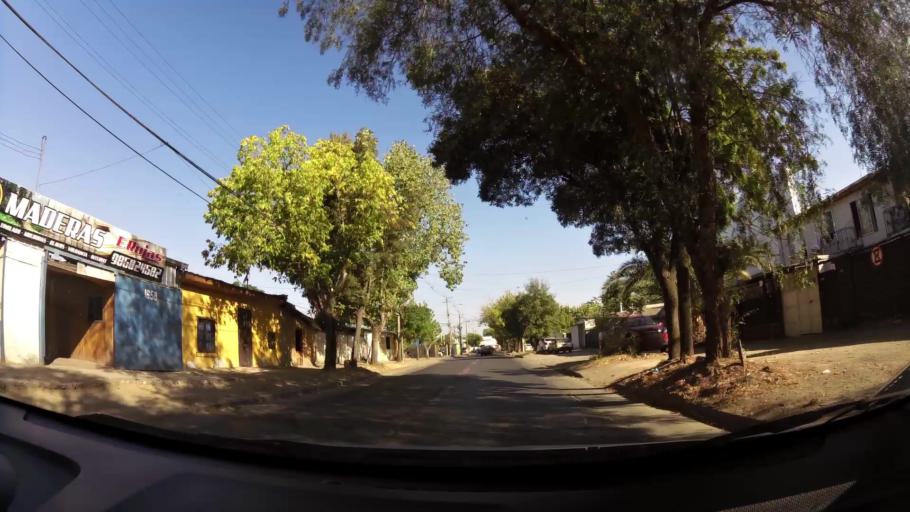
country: CL
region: Maule
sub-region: Provincia de Talca
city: Talca
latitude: -35.4205
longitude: -71.6513
